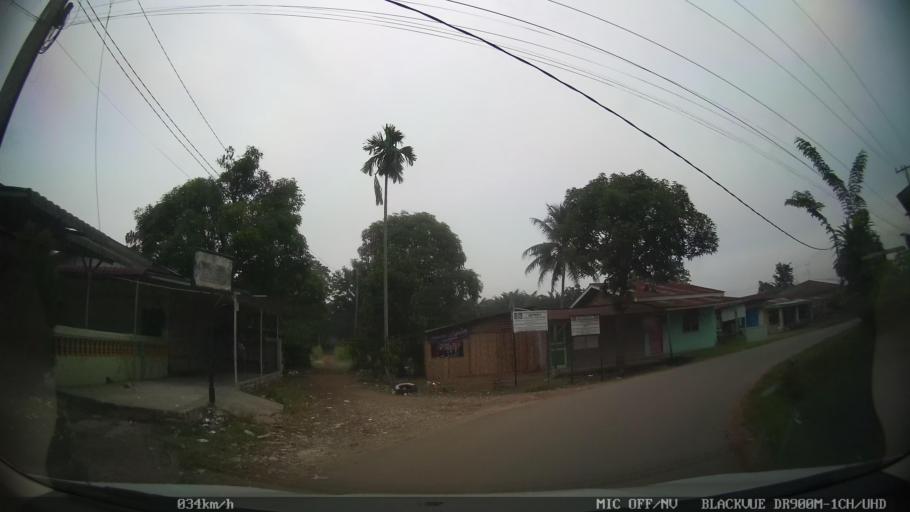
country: ID
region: North Sumatra
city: Deli Tua
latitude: 3.5431
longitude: 98.7284
